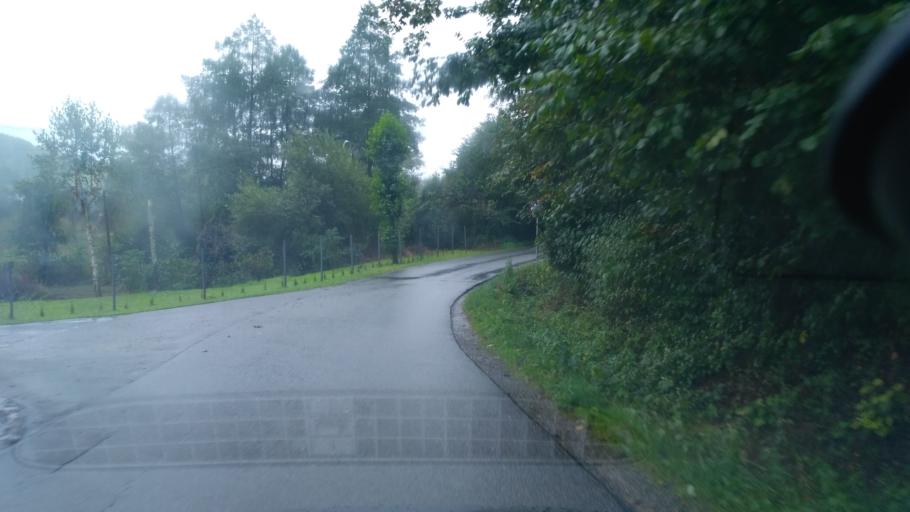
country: PL
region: Subcarpathian Voivodeship
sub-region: Powiat ropczycko-sedziszowski
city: Niedzwiada
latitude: 50.0098
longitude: 21.5486
